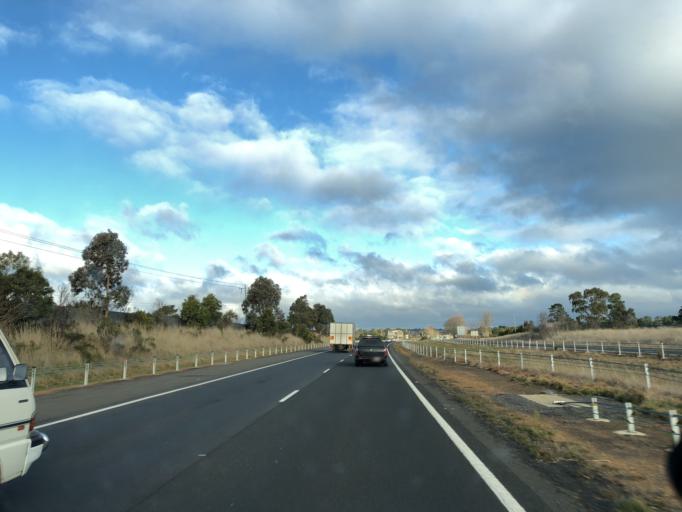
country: AU
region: Victoria
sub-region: Mount Alexander
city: Castlemaine
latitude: -37.2086
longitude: 144.4115
